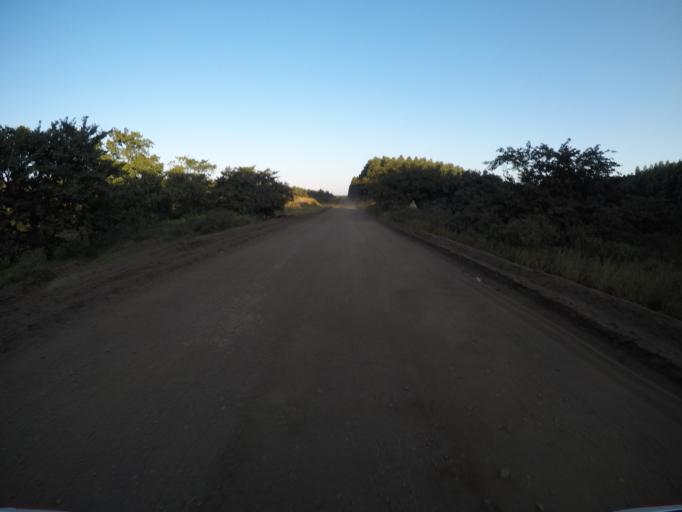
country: ZA
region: KwaZulu-Natal
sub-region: uThungulu District Municipality
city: KwaMbonambi
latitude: -28.6777
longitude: 32.1198
